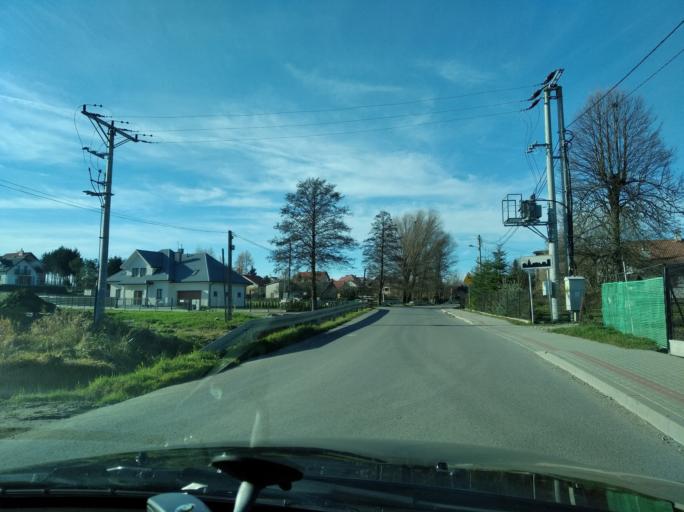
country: PL
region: Subcarpathian Voivodeship
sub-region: Powiat rzeszowski
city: Kielanowka
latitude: 50.0105
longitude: 21.9373
